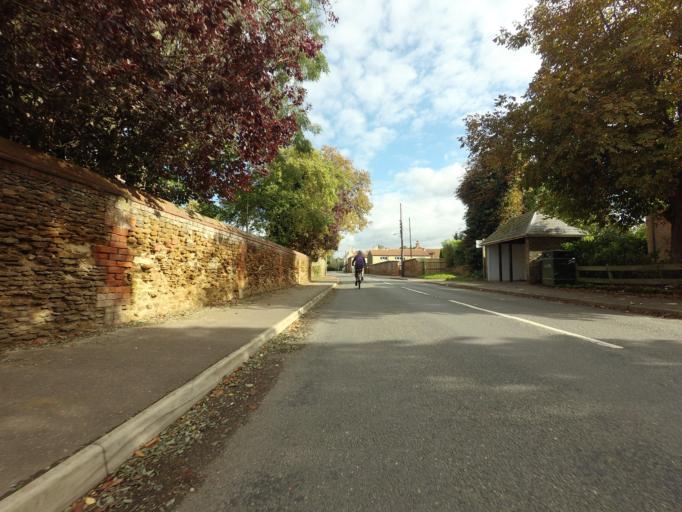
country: GB
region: England
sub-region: Norfolk
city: Dersingham
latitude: 52.8461
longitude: 0.5095
